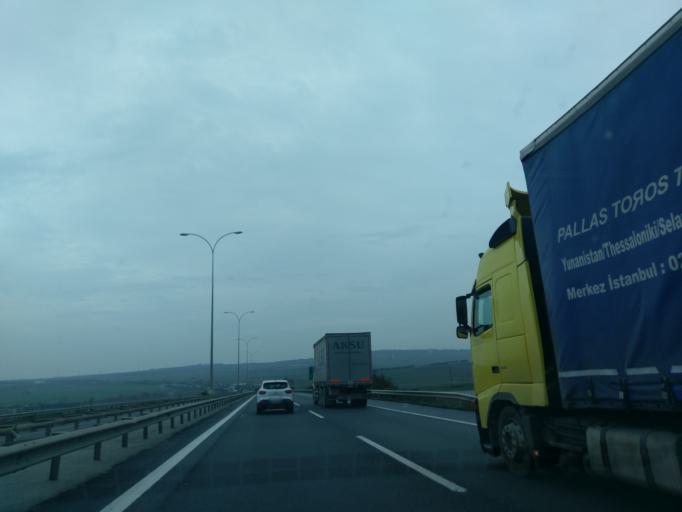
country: TR
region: Istanbul
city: Silivri
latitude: 41.1151
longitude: 28.2587
